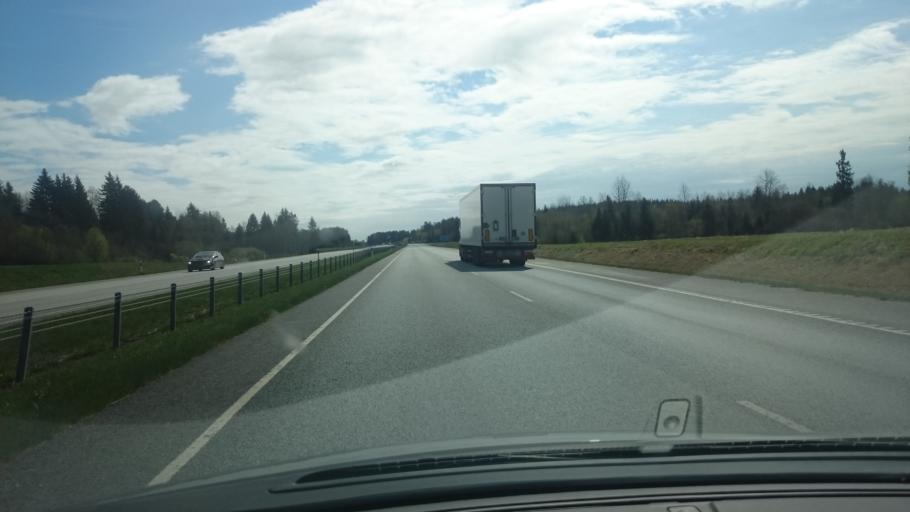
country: EE
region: Laeaene-Virumaa
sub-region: Kadrina vald
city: Kadrina
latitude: 59.4515
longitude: 26.0630
